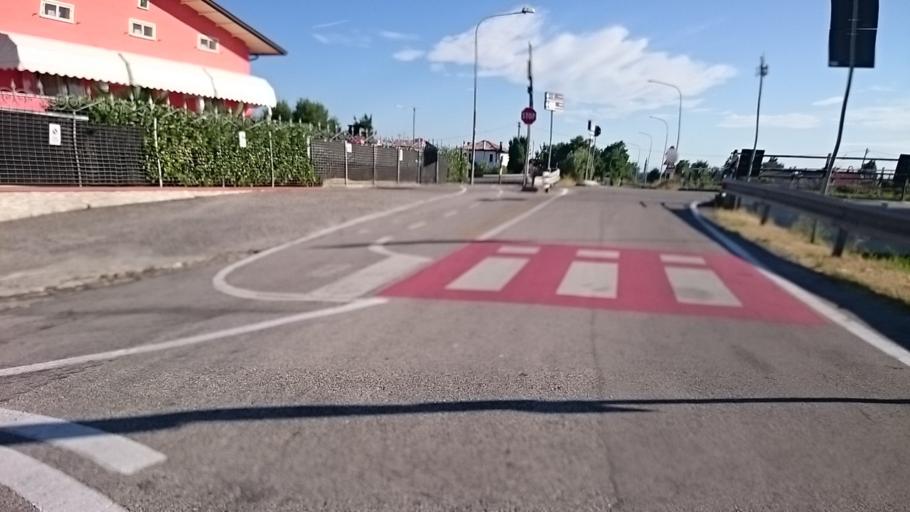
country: IT
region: Veneto
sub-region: Provincia di Padova
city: Mejaniga
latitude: 45.4824
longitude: 11.8993
